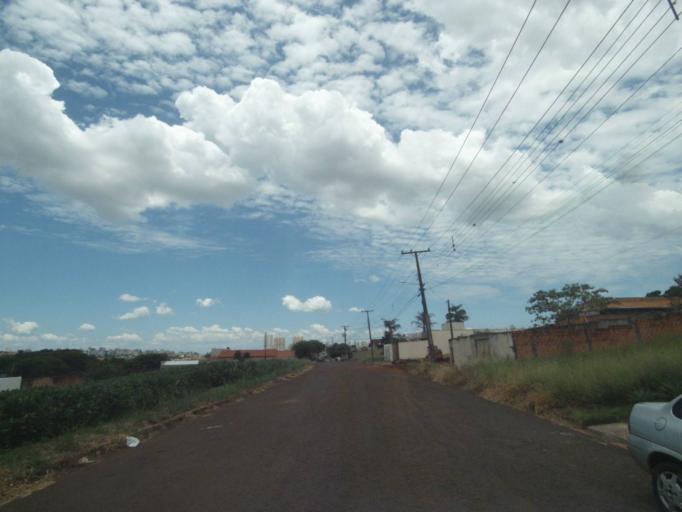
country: BR
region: Parana
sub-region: Londrina
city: Londrina
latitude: -23.3191
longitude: -51.2062
